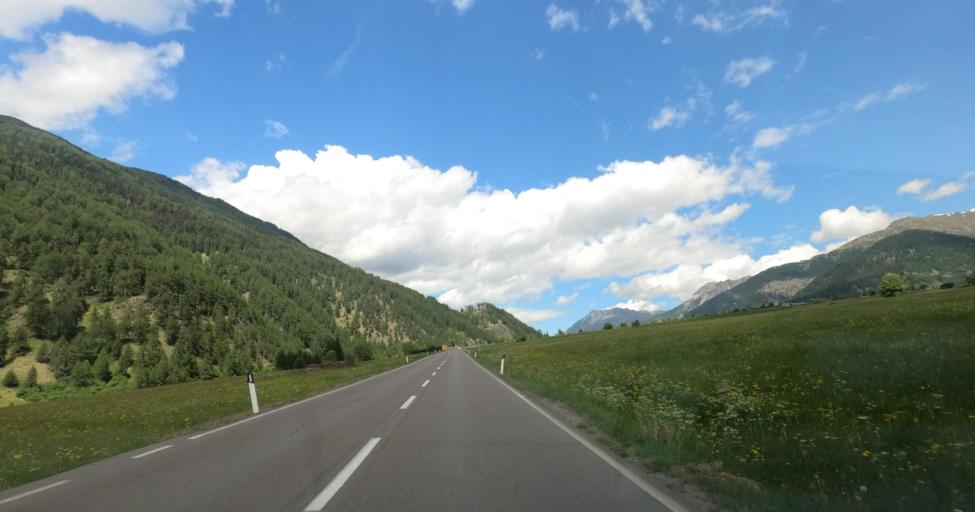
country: IT
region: Trentino-Alto Adige
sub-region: Bolzano
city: Malles Venosta
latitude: 46.7214
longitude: 10.5337
